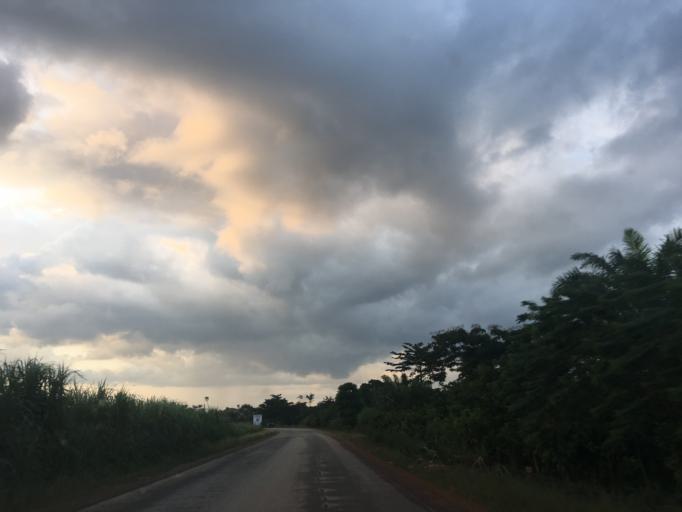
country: GH
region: Western
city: Bibiani
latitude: 6.7584
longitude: -2.5041
